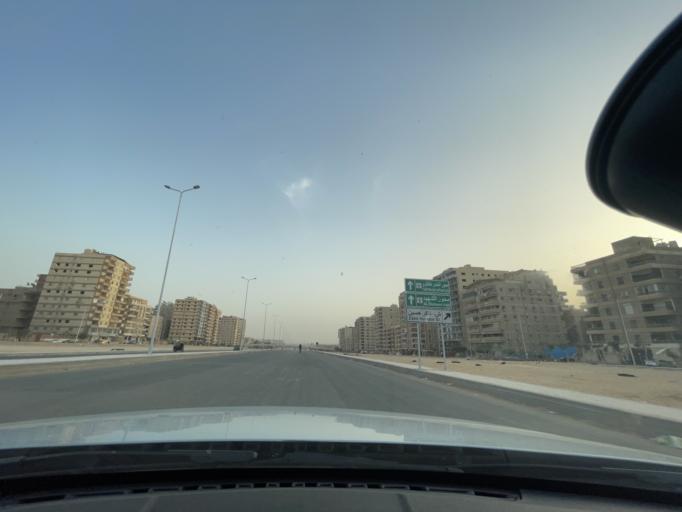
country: EG
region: Muhafazat al Qahirah
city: Cairo
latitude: 30.0519
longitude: 31.3697
